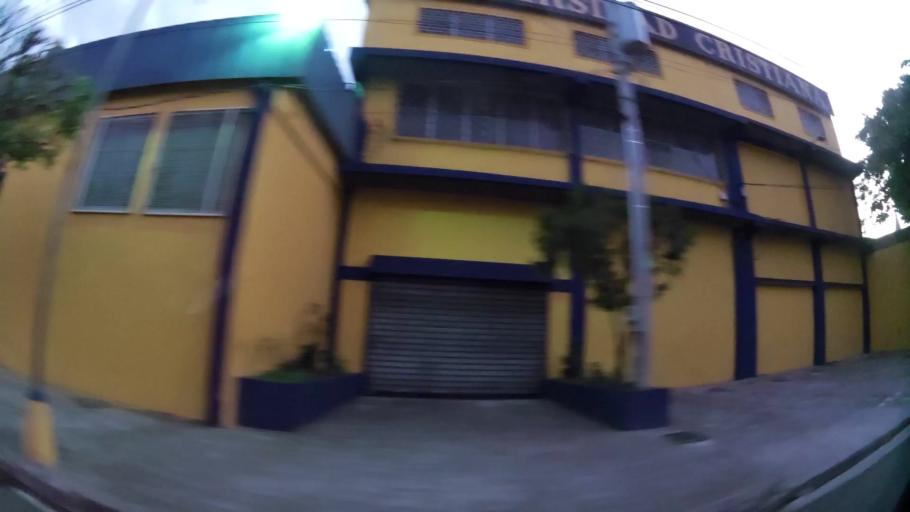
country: SV
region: San Salvador
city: Delgado
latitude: 13.7123
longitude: -89.1889
